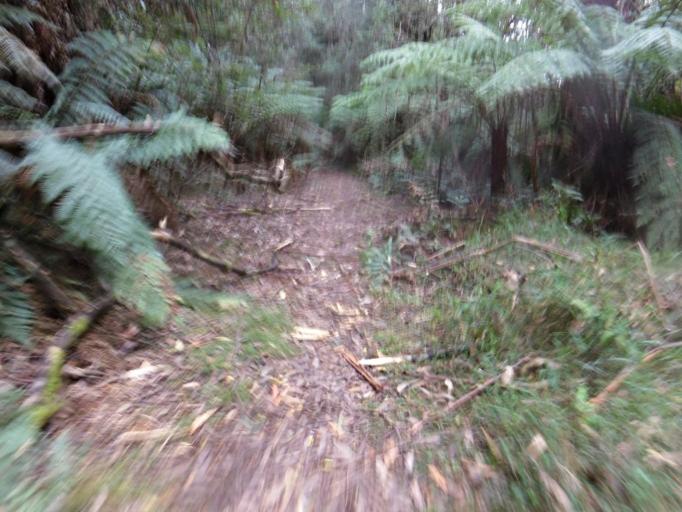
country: AU
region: Victoria
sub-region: Yarra Ranges
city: Healesville
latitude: -37.5143
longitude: 145.5196
